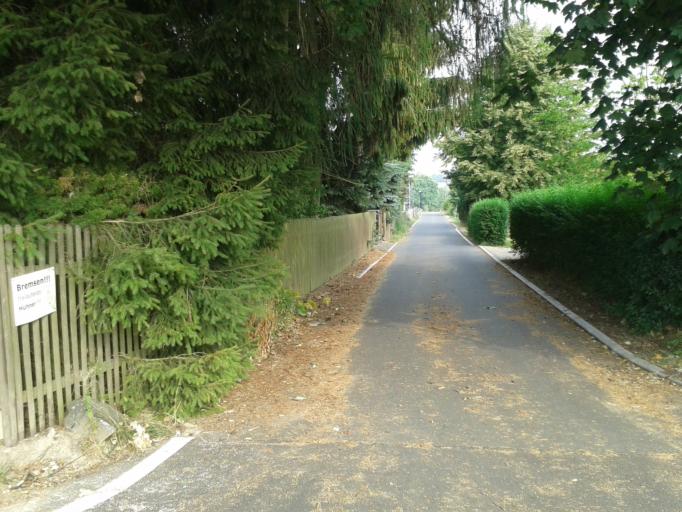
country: DE
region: Saxony
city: Oederan
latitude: 50.8777
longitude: 13.1461
